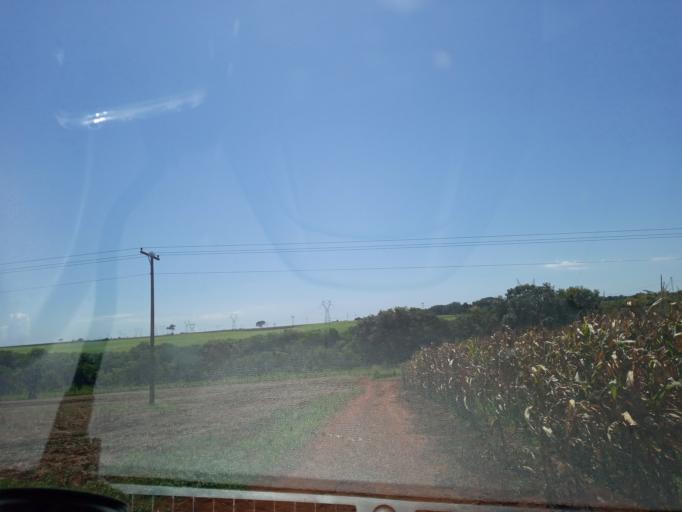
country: BR
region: Goias
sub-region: Itumbiara
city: Itumbiara
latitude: -18.4448
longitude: -49.1439
